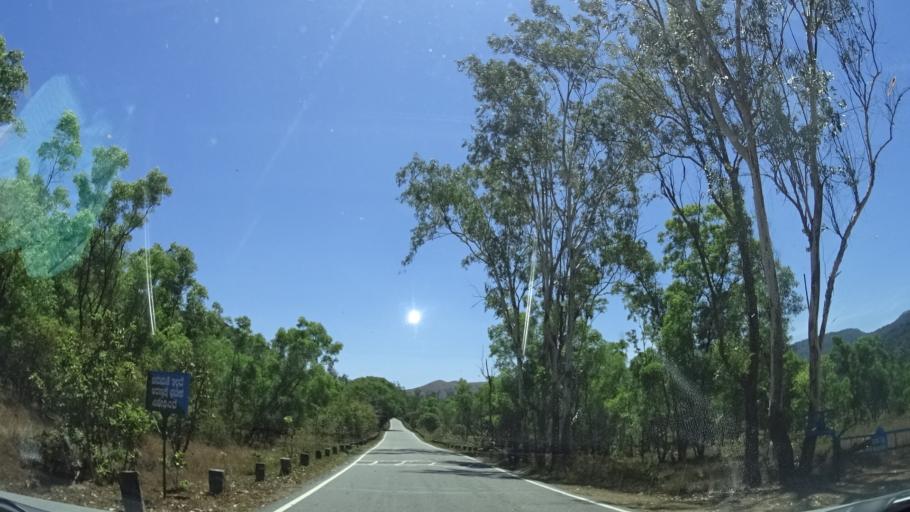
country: IN
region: Karnataka
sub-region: Udupi
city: Karkal
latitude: 13.2114
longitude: 75.1870
